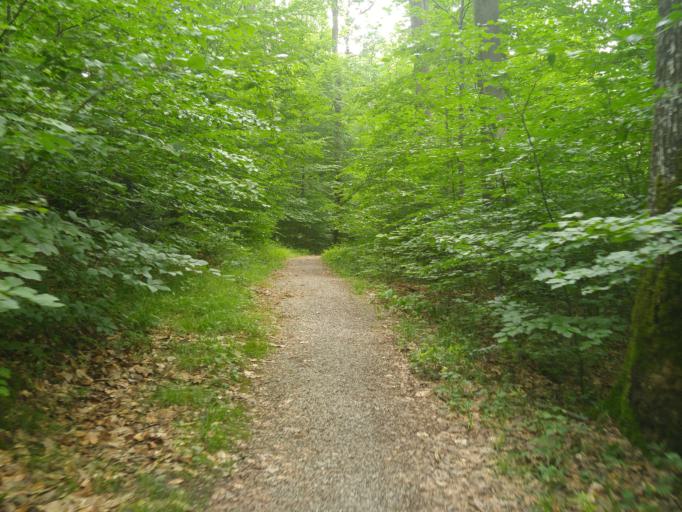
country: DE
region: Baden-Wuerttemberg
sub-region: Regierungsbezirk Stuttgart
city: Wustenrot
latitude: 49.0782
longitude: 9.4482
